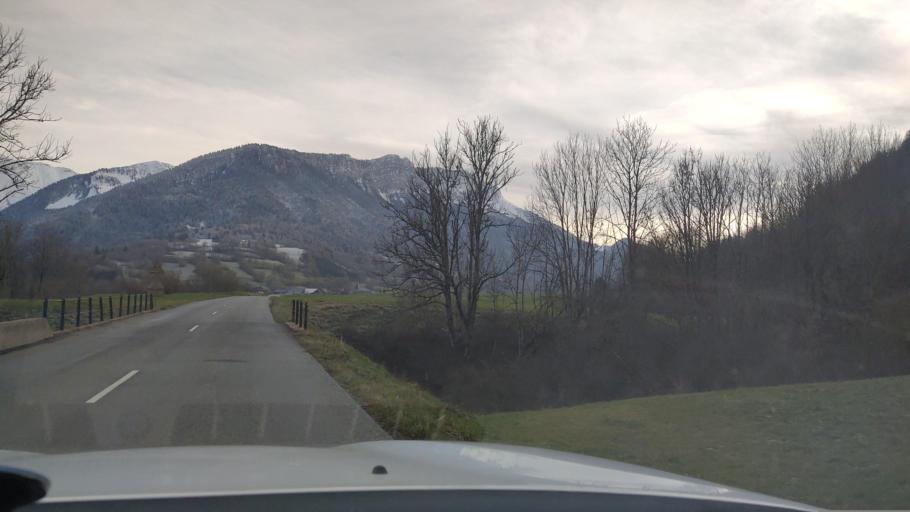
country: FR
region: Rhone-Alpes
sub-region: Departement de la Savoie
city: Gresy-sur-Isere
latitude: 45.6578
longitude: 6.1632
